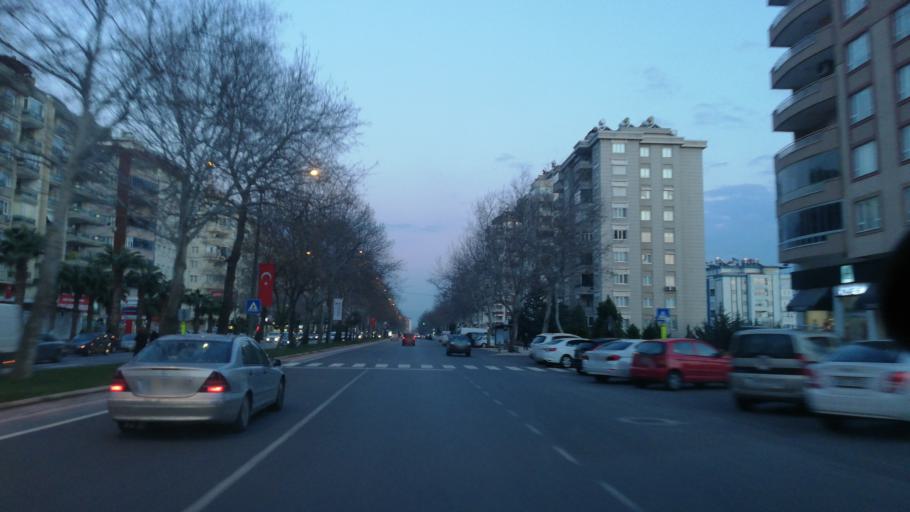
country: TR
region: Kahramanmaras
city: Kahramanmaras
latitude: 37.5878
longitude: 36.8901
